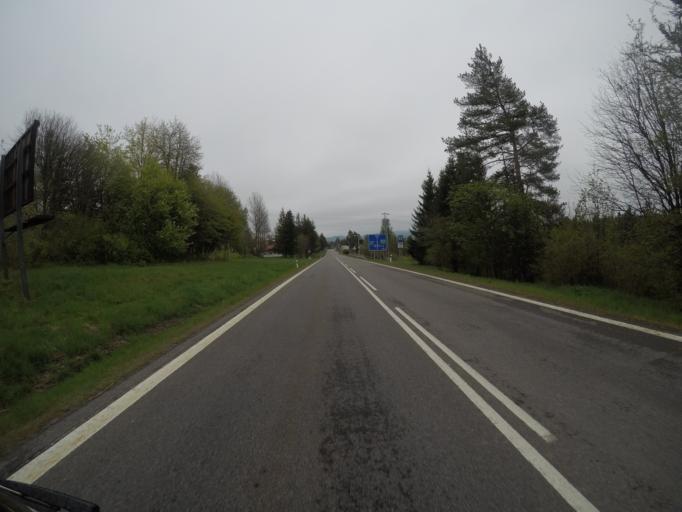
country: SK
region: Presovsky
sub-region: Okres Poprad
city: Strba
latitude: 49.0852
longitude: 20.0646
